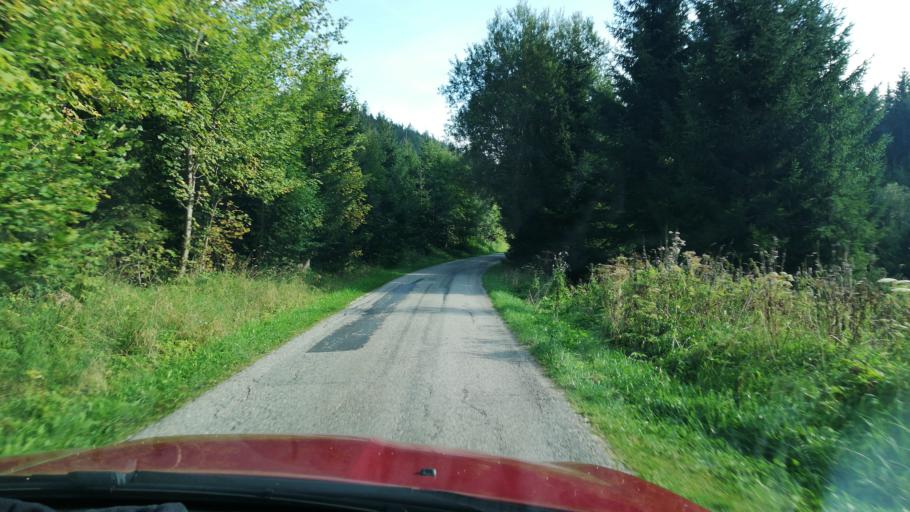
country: AT
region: Lower Austria
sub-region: Politischer Bezirk Zwettl
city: Langschlag
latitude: 48.4808
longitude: 14.8401
